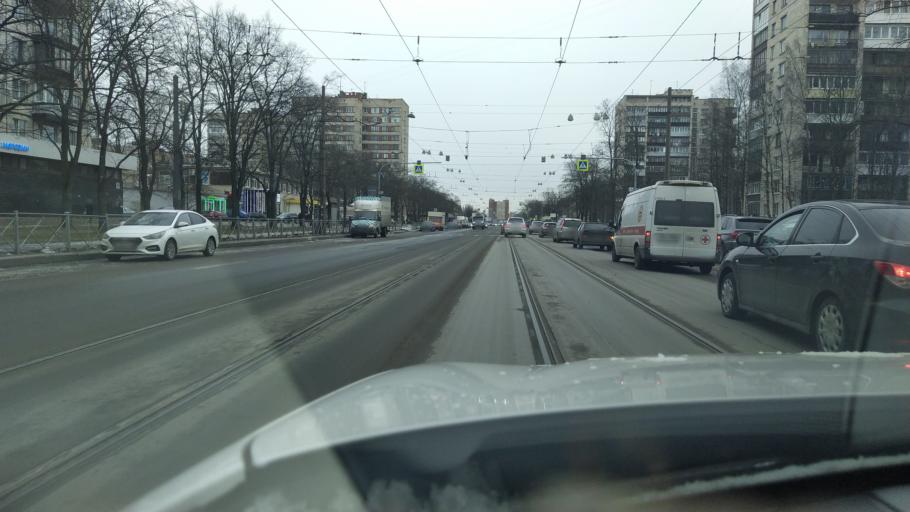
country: RU
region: Leningrad
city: Akademicheskoe
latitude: 60.0079
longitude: 30.4184
